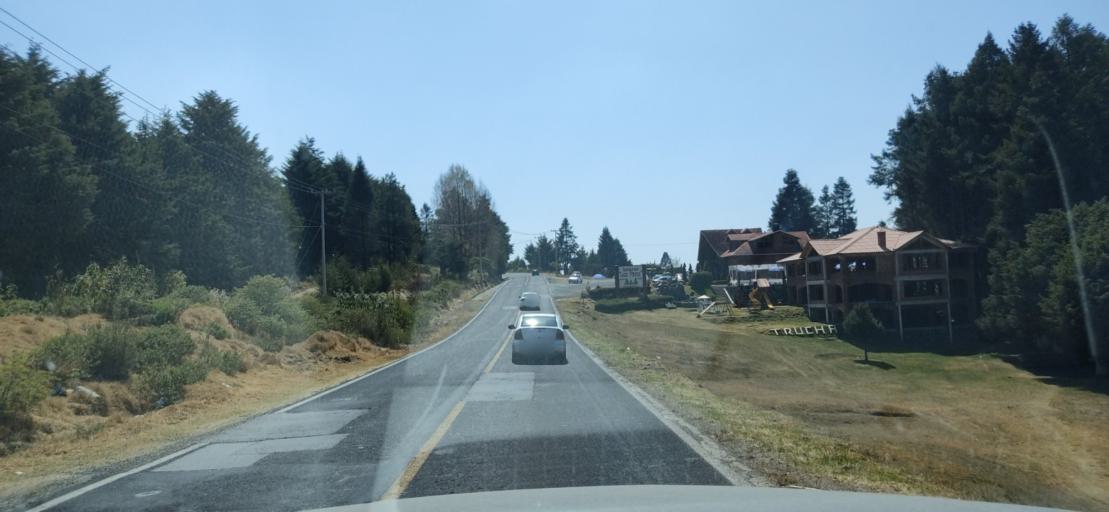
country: MX
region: Mexico
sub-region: Ocoyoacac
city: San Jeronimo Acazulco
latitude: 19.2670
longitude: -99.3764
